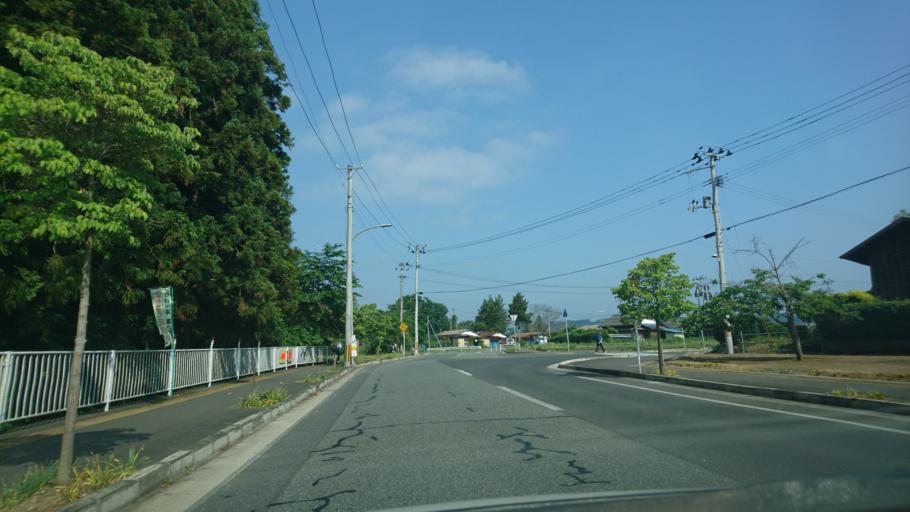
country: JP
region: Iwate
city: Ichinoseki
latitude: 38.9290
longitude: 141.1127
